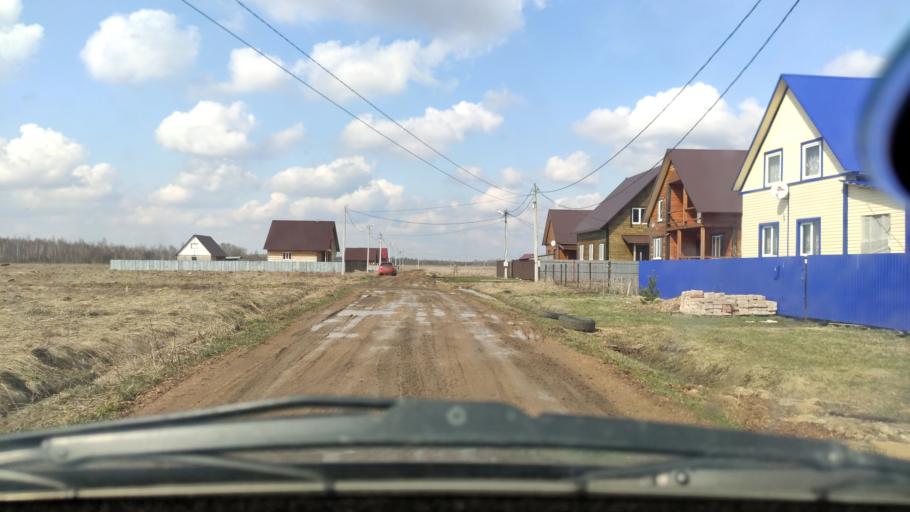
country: RU
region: Bashkortostan
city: Iglino
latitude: 54.8253
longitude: 56.3709
